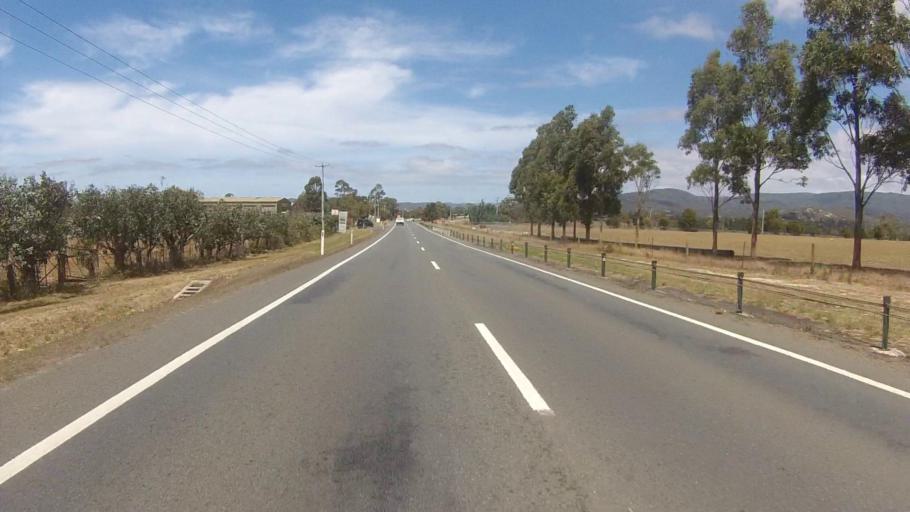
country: AU
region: Tasmania
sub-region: Kingborough
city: Margate
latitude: -43.0121
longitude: 147.2720
